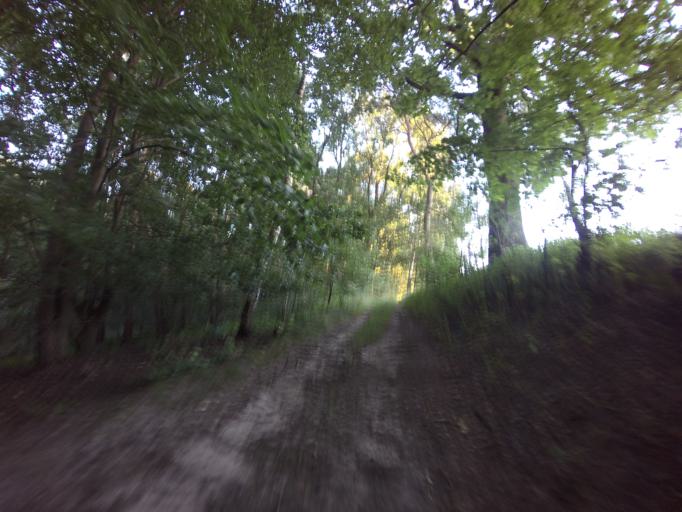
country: PL
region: West Pomeranian Voivodeship
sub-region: Powiat choszczenski
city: Choszczno
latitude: 53.2103
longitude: 15.4226
